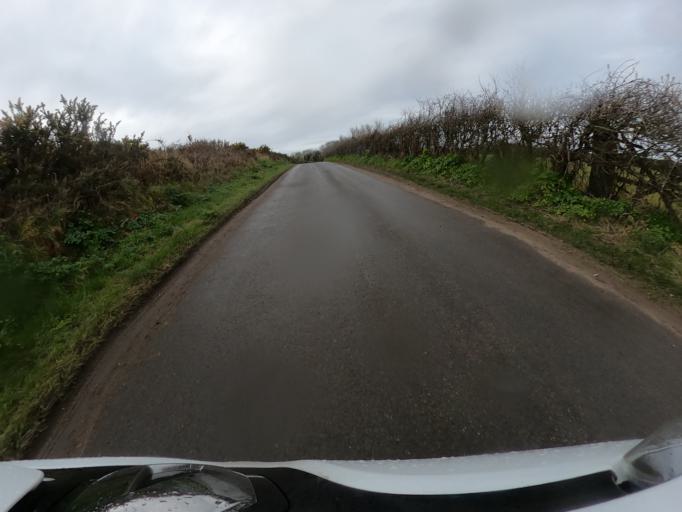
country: IM
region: Ramsey
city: Ramsey
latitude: 54.3815
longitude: -4.4629
